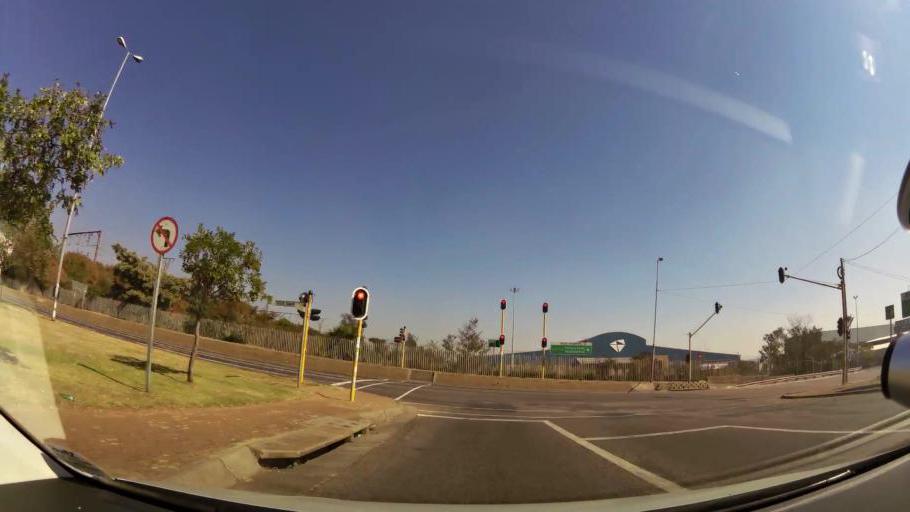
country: ZA
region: Gauteng
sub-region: City of Tshwane Metropolitan Municipality
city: Pretoria
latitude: -25.7550
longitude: 28.1816
